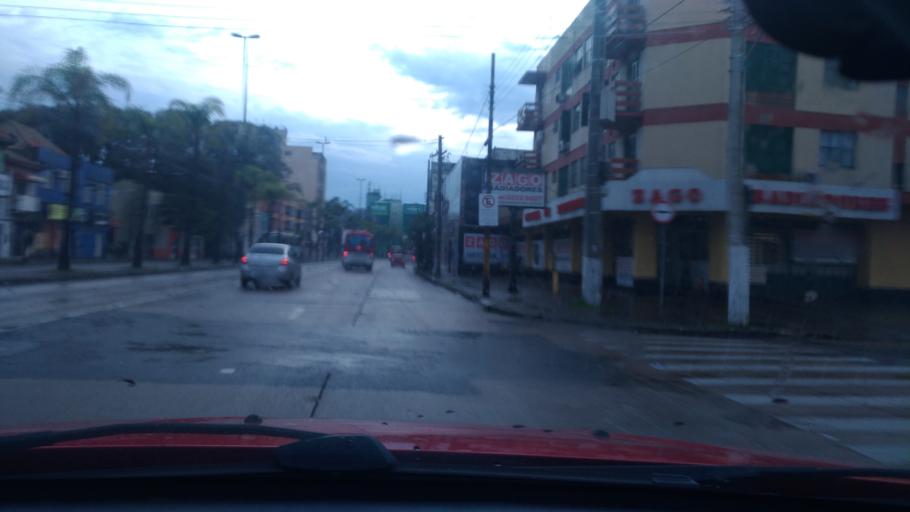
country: BR
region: Rio Grande do Sul
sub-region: Porto Alegre
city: Porto Alegre
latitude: -30.0195
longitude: -51.2100
